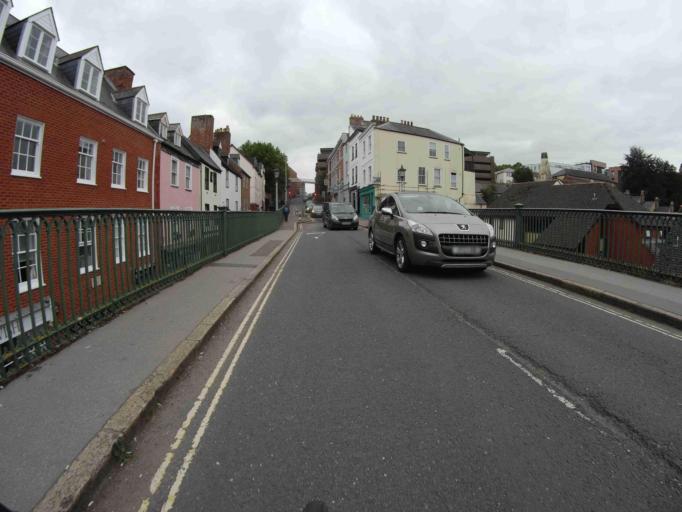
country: GB
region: England
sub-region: Devon
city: Exeter
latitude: 50.7241
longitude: -3.5354
